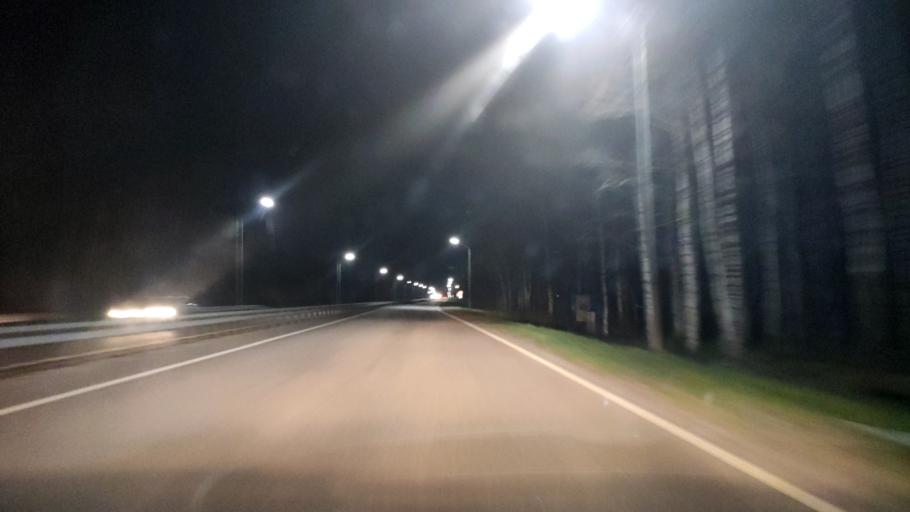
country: RU
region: Belgorod
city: Staryy Oskol
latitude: 51.4112
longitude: 37.8840
